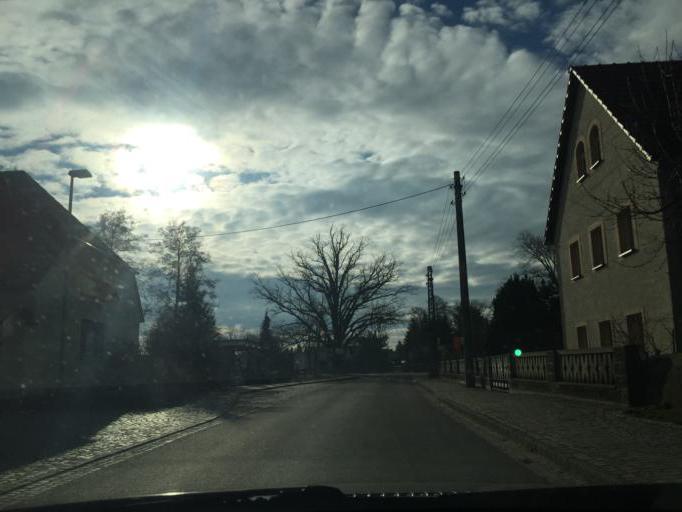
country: DE
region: Saxony
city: Ebersbach
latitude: 51.2369
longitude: 13.6604
